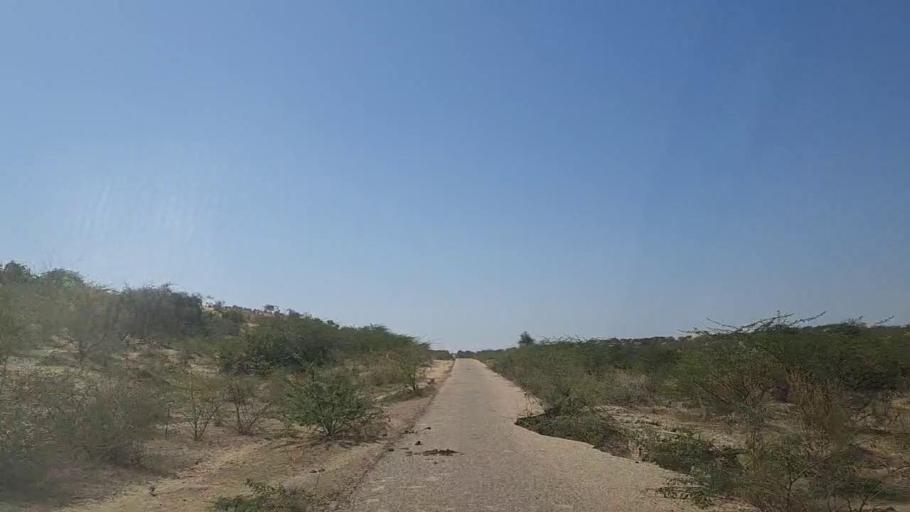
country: PK
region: Sindh
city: Mithi
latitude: 24.8232
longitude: 69.6742
